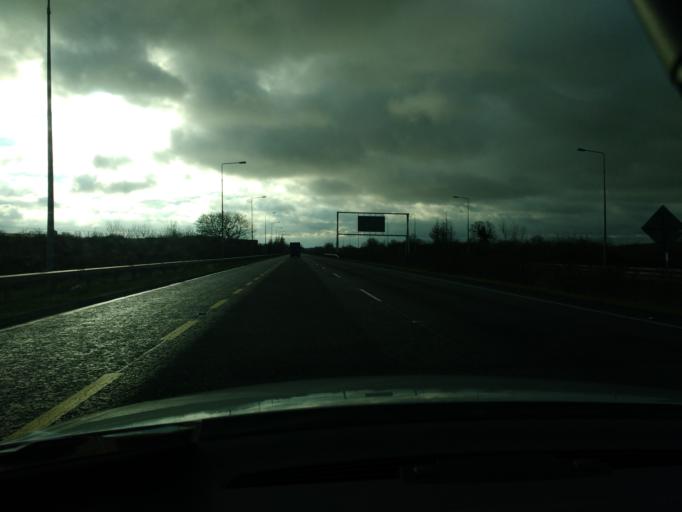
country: IE
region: Munster
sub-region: An Clar
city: Shannon
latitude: 52.7222
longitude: -8.8775
